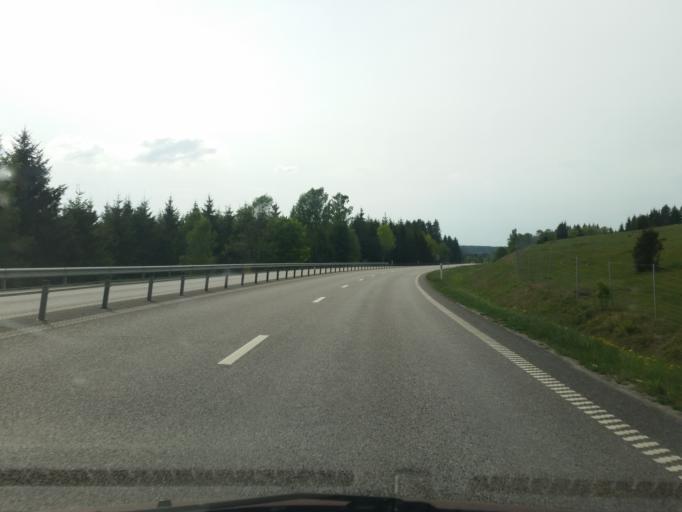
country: SE
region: Vaestra Goetaland
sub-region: Ulricehamns Kommun
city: Ulricehamn
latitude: 57.8001
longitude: 13.3876
